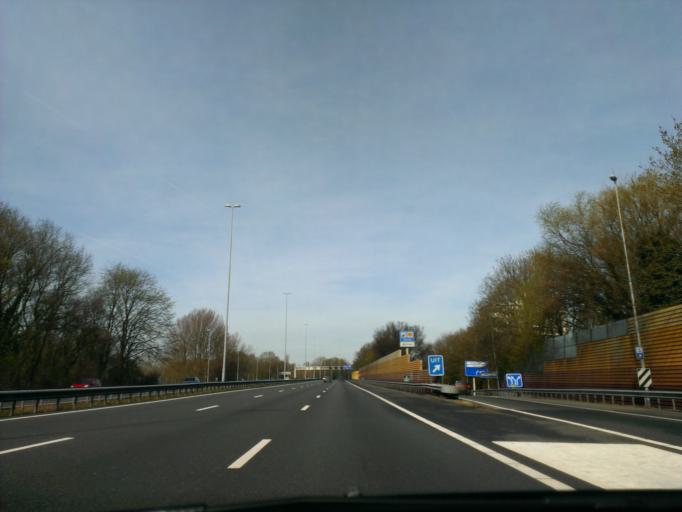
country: NL
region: North Holland
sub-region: Gemeente Amstelveen
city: Amstelveen
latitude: 52.3007
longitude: 4.8601
